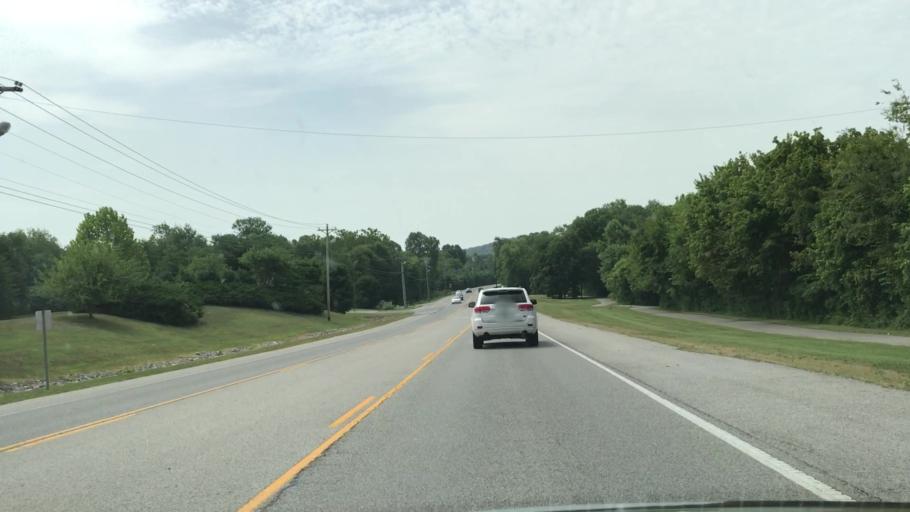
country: US
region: Tennessee
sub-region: Williamson County
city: Brentwood Estates
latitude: 35.9551
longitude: -86.7670
